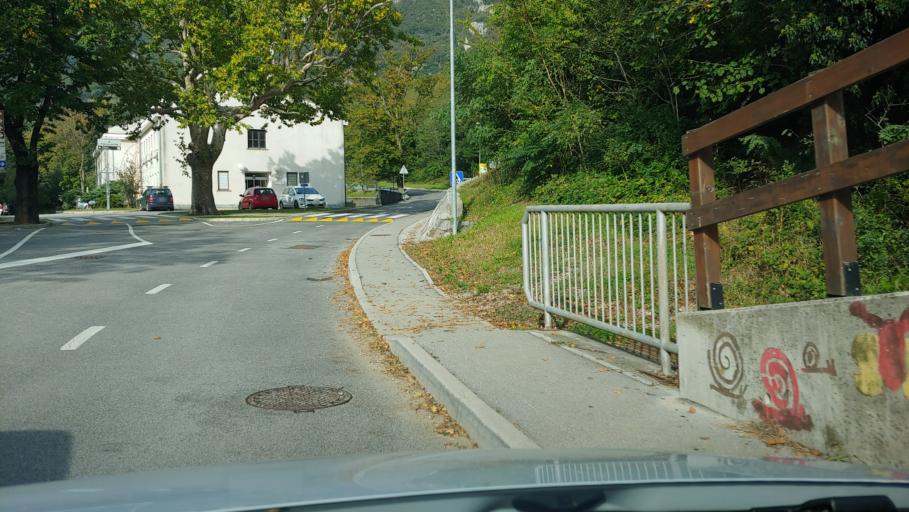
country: SI
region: Ajdovscina
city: Ajdovscina
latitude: 45.8955
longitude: 13.9064
